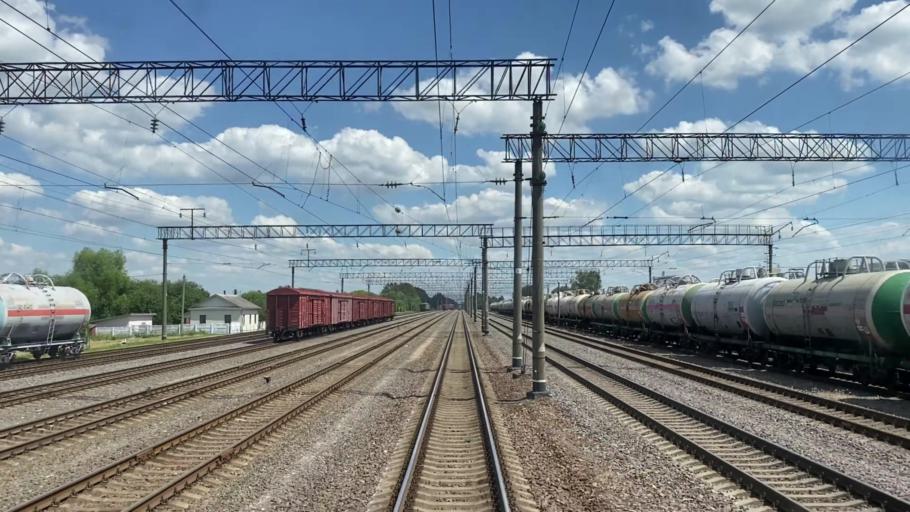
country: BY
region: Brest
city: Byaroza
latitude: 52.5355
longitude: 24.9120
